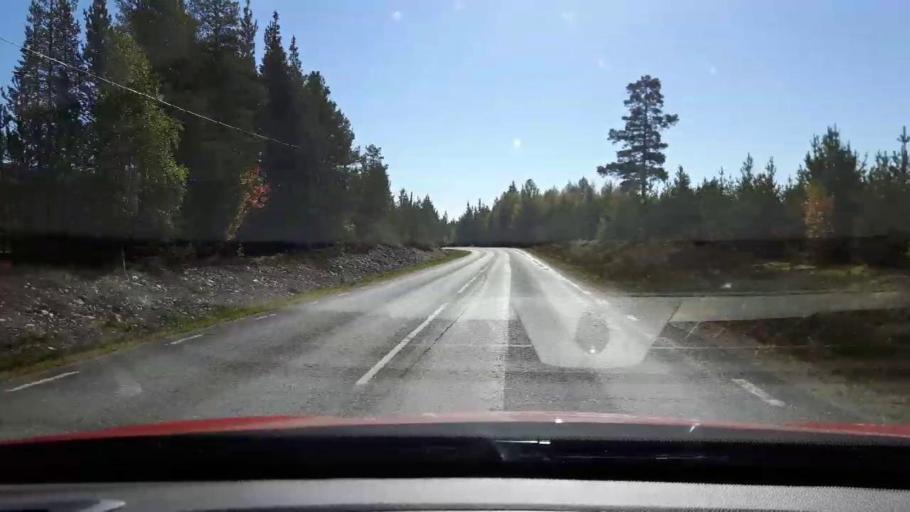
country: SE
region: Jaemtland
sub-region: Harjedalens Kommun
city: Sveg
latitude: 62.4285
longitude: 13.8927
